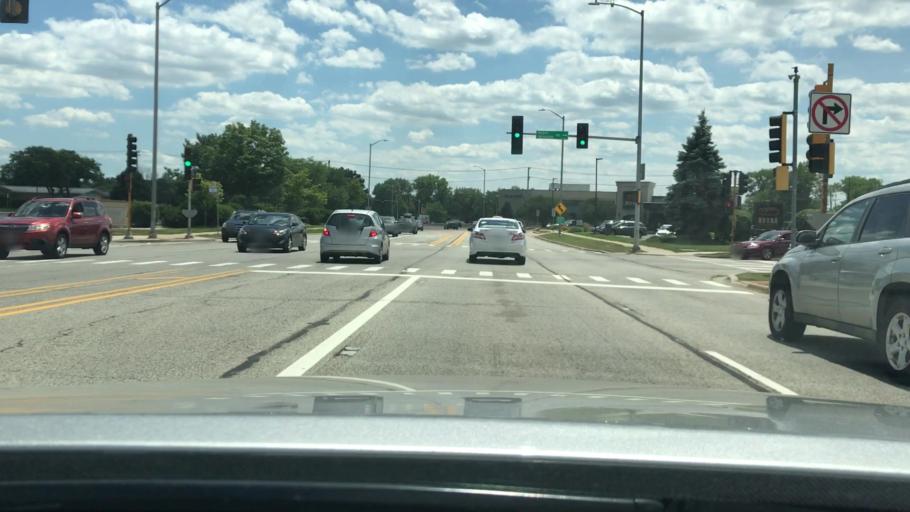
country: US
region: Illinois
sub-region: DuPage County
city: Naperville
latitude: 41.7998
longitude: -88.1200
